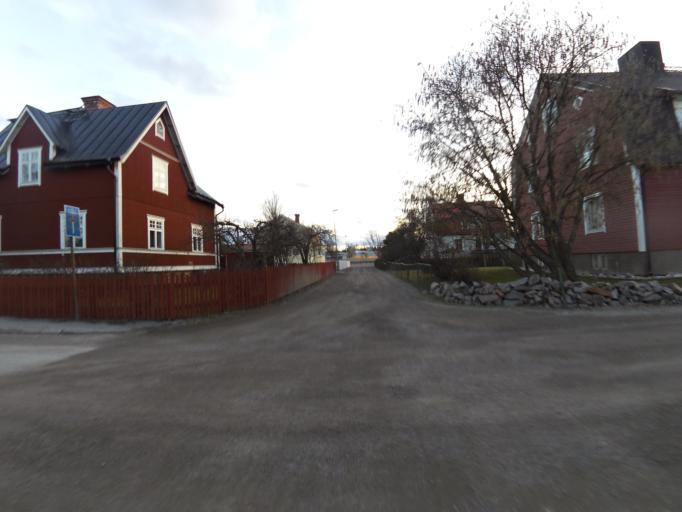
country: SE
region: Gaevleborg
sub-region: Gavle Kommun
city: Gavle
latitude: 60.6615
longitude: 17.1629
